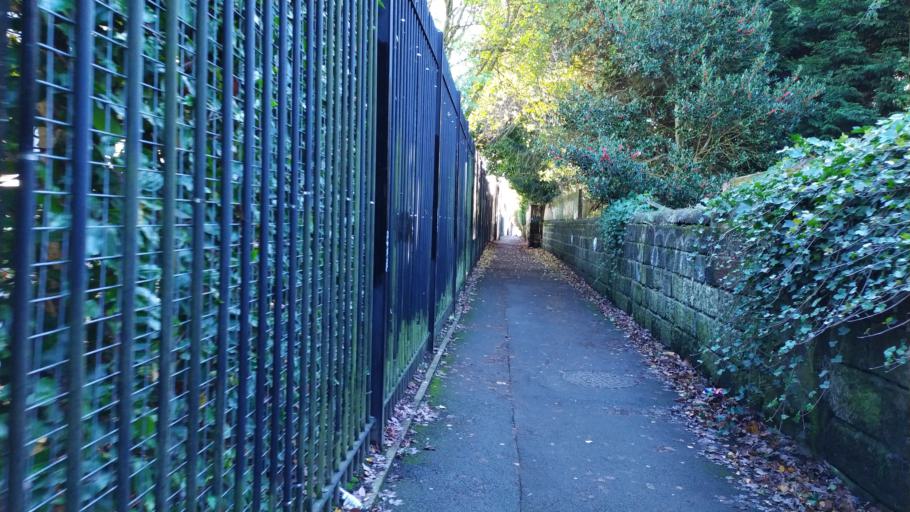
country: GB
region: England
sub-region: City and Borough of Leeds
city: Leeds
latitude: 53.8174
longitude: -1.5835
